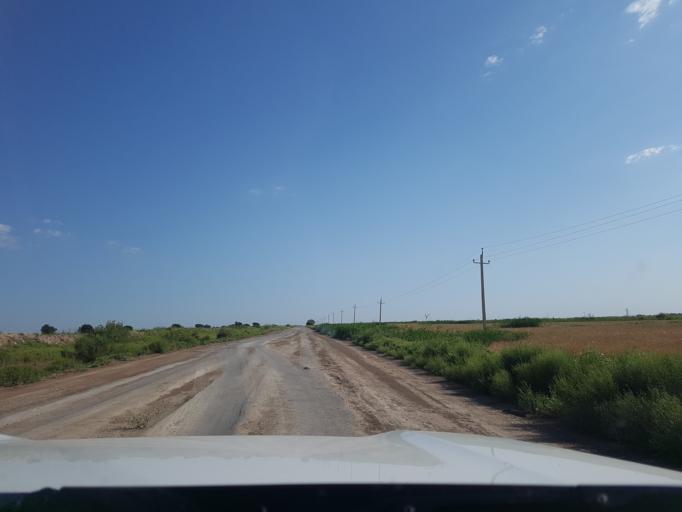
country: TM
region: Dasoguz
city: Koeneuergench
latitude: 41.9244
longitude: 58.7124
